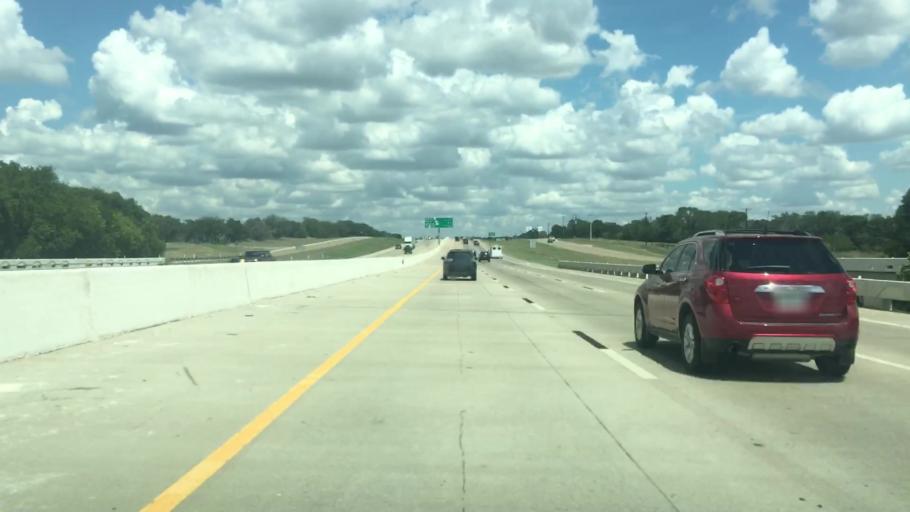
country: US
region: Texas
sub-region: Bell County
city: Belton
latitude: 31.0015
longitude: -97.4920
